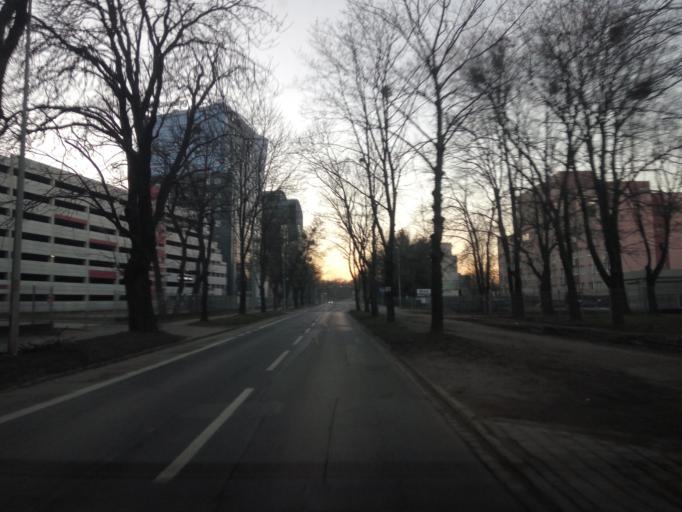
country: PL
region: Lower Silesian Voivodeship
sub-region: Powiat wroclawski
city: Wroclaw
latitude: 51.1137
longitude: 16.9965
